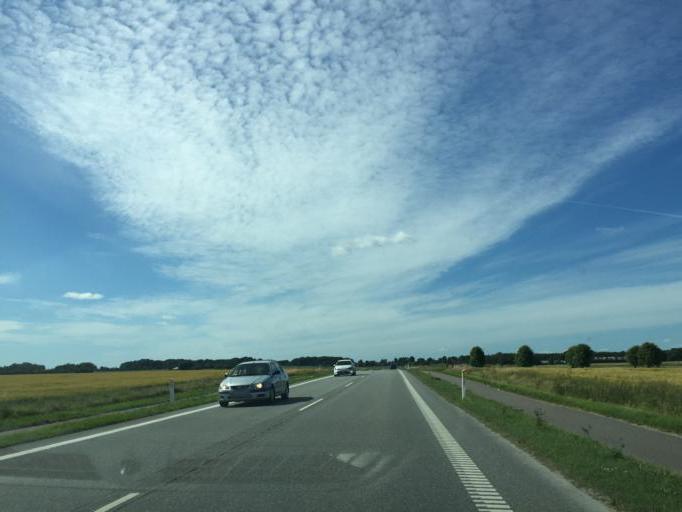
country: DK
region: South Denmark
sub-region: Odense Kommune
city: Hojby
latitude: 55.3366
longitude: 10.3867
